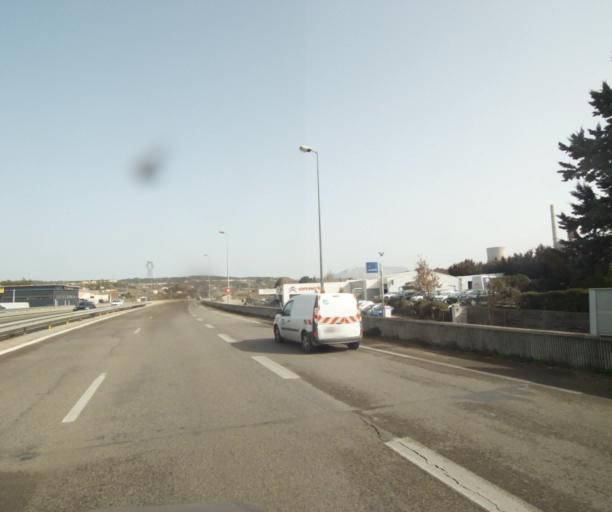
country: FR
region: Provence-Alpes-Cote d'Azur
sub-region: Departement des Bouches-du-Rhone
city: Gardanne
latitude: 43.4664
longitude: 5.4669
